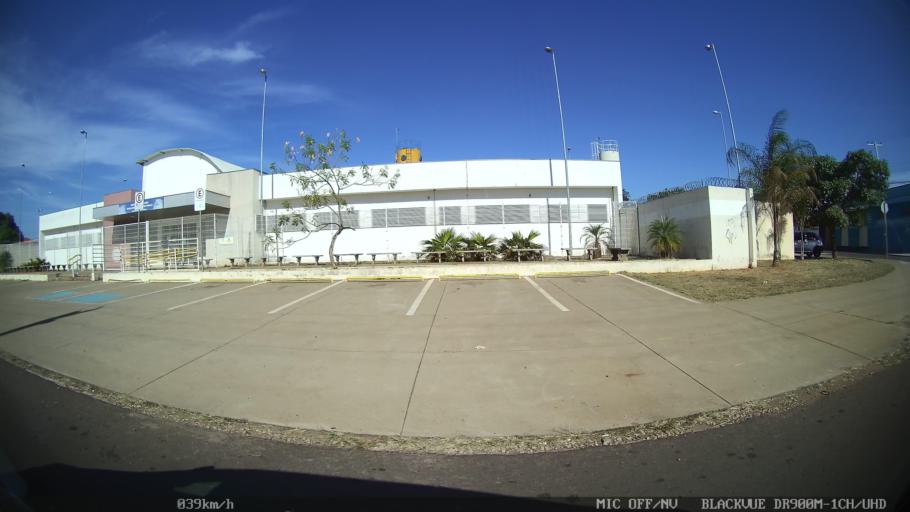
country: BR
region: Sao Paulo
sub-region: Franca
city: Franca
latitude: -20.4876
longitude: -47.4204
